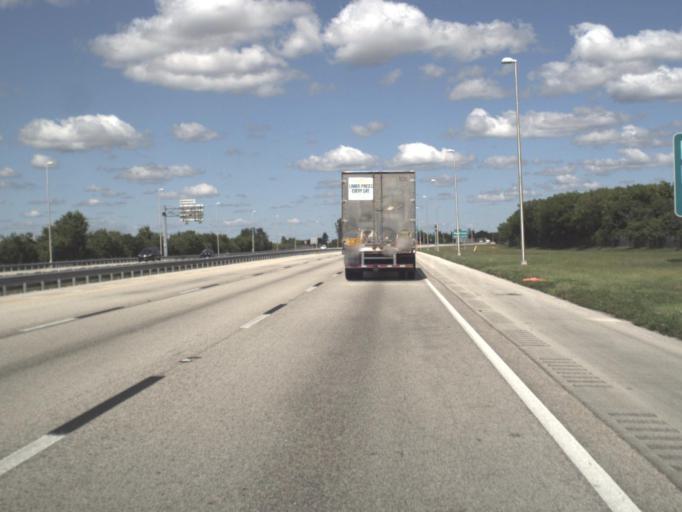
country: US
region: Florida
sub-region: Broward County
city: Coral Springs
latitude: 26.2914
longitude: -80.2970
